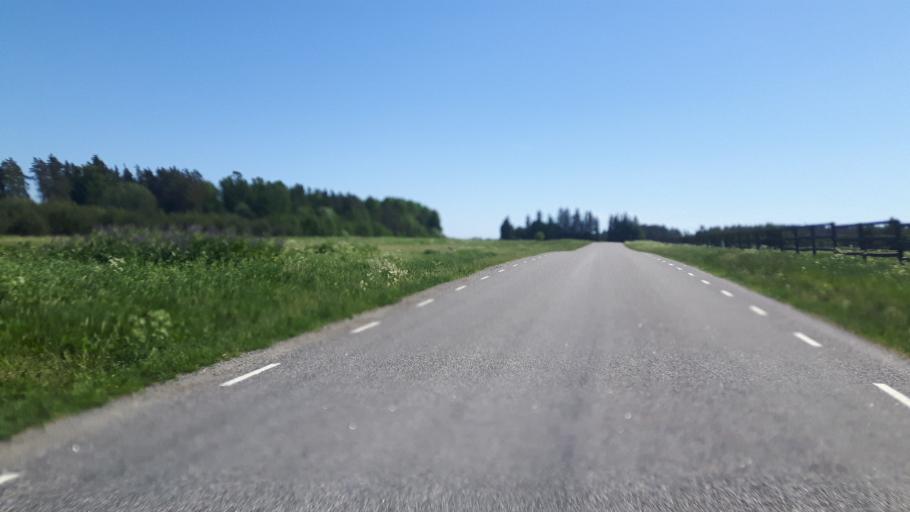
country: EE
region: Raplamaa
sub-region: Kohila vald
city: Kohila
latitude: 59.1989
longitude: 24.6945
